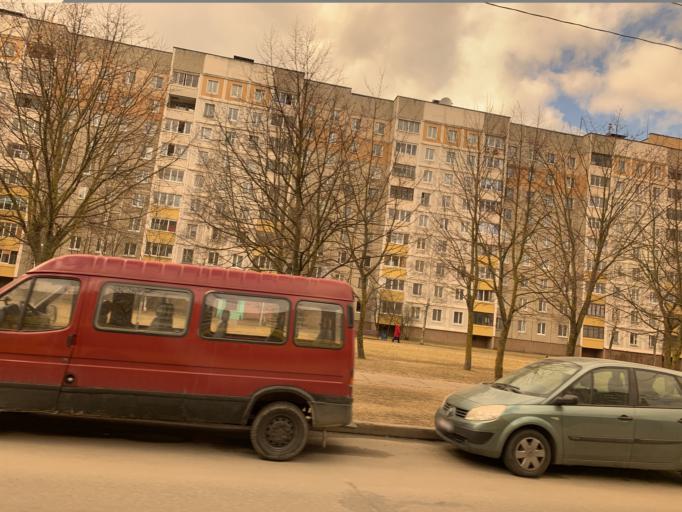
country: BY
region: Minsk
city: Borovlyany
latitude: 53.9371
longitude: 27.6873
